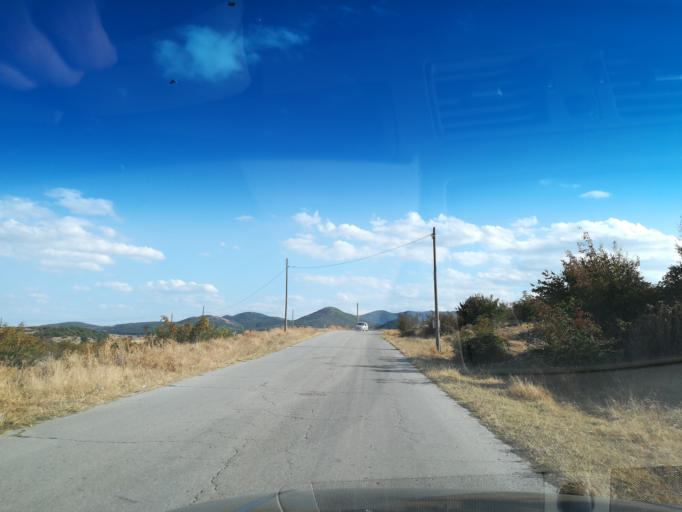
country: BG
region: Khaskovo
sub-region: Obshtina Mineralni Bani
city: Mineralni Bani
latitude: 41.9692
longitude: 25.3007
